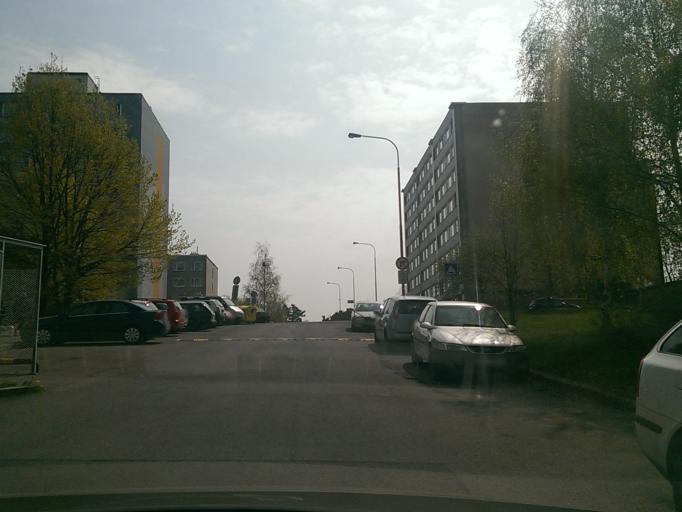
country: CZ
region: Central Bohemia
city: Vestec
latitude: 50.0430
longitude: 14.4984
